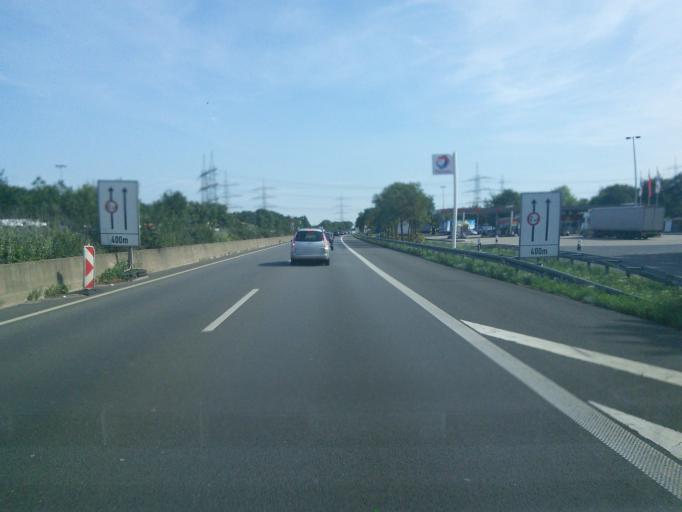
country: DE
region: North Rhine-Westphalia
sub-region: Regierungsbezirk Dusseldorf
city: Dormagen
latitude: 51.1251
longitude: 6.7955
